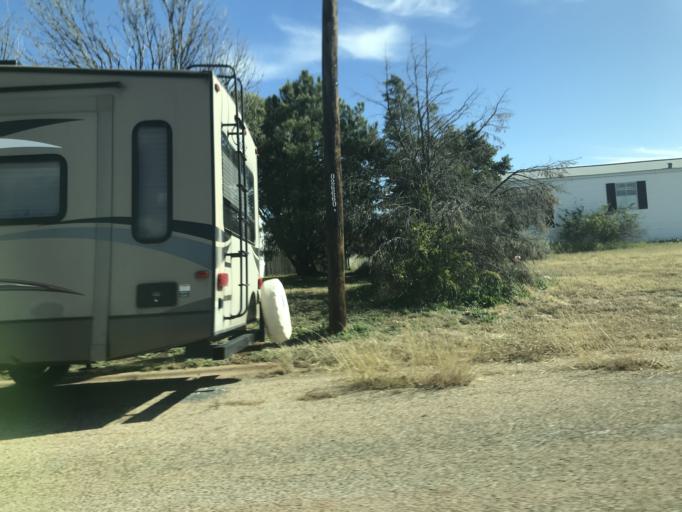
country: US
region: Texas
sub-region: Taylor County
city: Abilene
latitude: 32.5013
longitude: -99.7605
